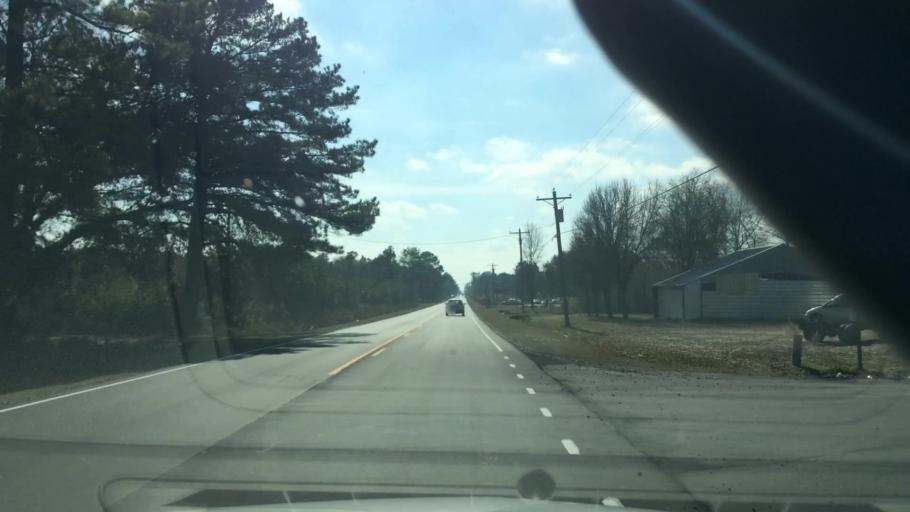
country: US
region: North Carolina
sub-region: Duplin County
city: Beulaville
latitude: 34.9924
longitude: -77.7571
